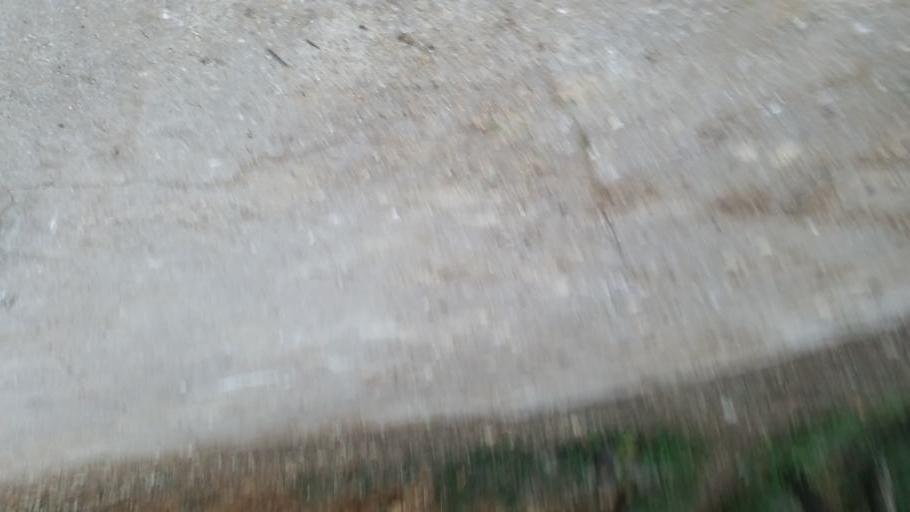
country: ES
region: Balearic Islands
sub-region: Illes Balears
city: Pollenca
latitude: 39.8694
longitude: 3.0183
